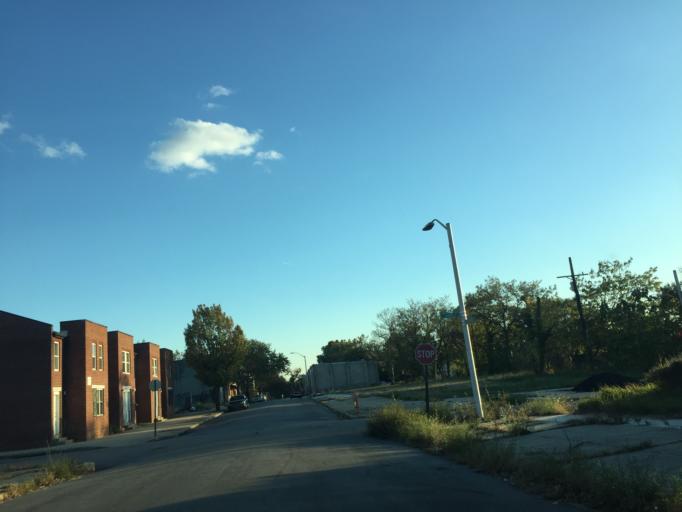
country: US
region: Maryland
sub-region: City of Baltimore
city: Baltimore
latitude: 39.3096
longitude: -76.6033
